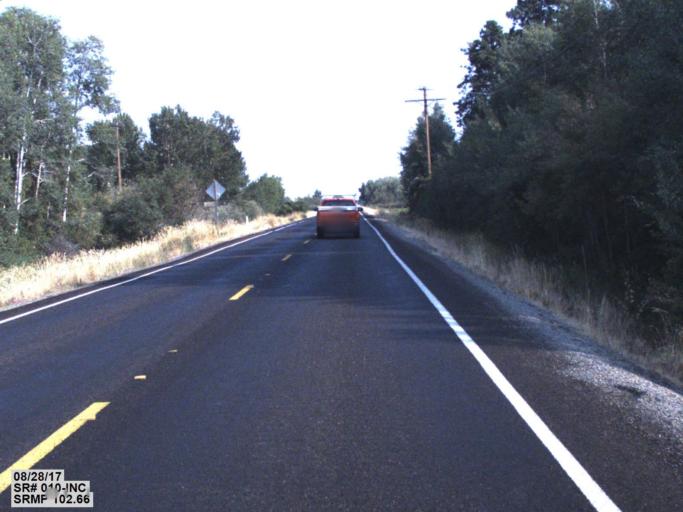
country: US
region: Washington
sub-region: Kittitas County
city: Ellensburg
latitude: 47.0529
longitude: -120.6375
